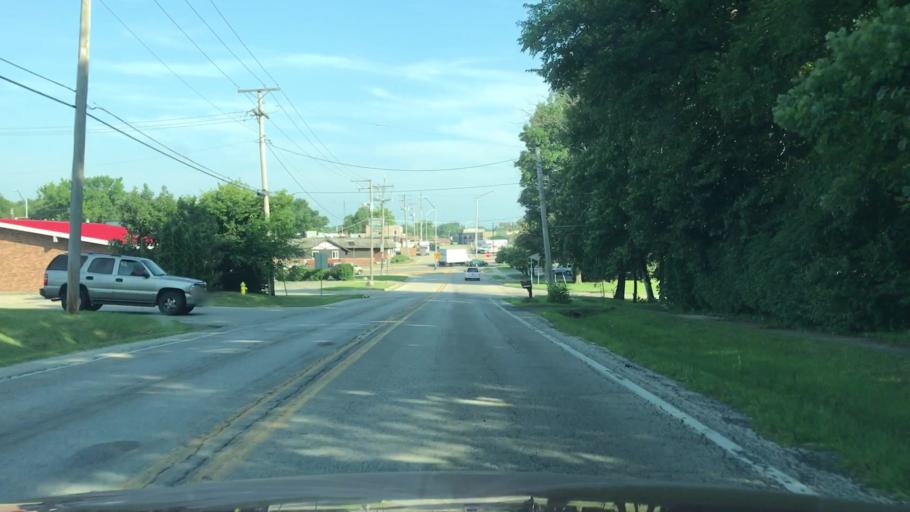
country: US
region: Illinois
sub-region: Winnebago County
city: Rockford
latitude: 42.2509
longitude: -89.0276
